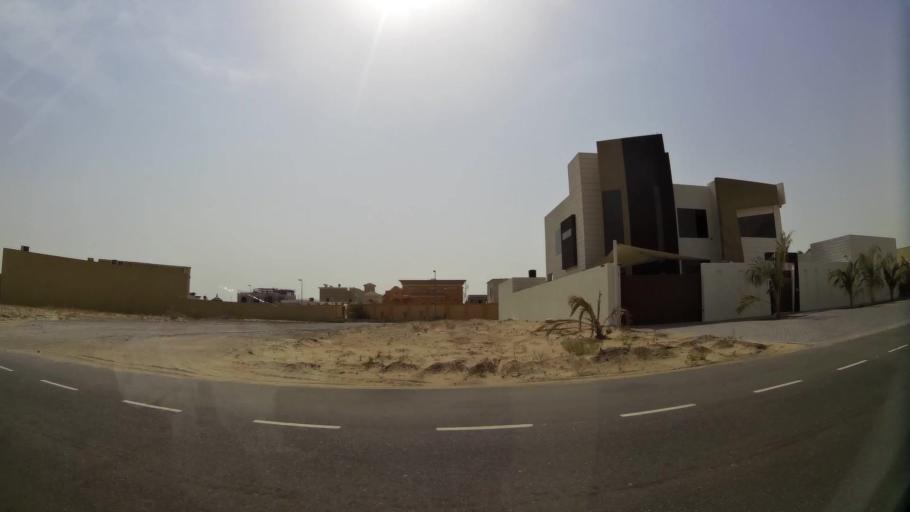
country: AE
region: Ash Shariqah
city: Sharjah
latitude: 25.2579
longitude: 55.4629
